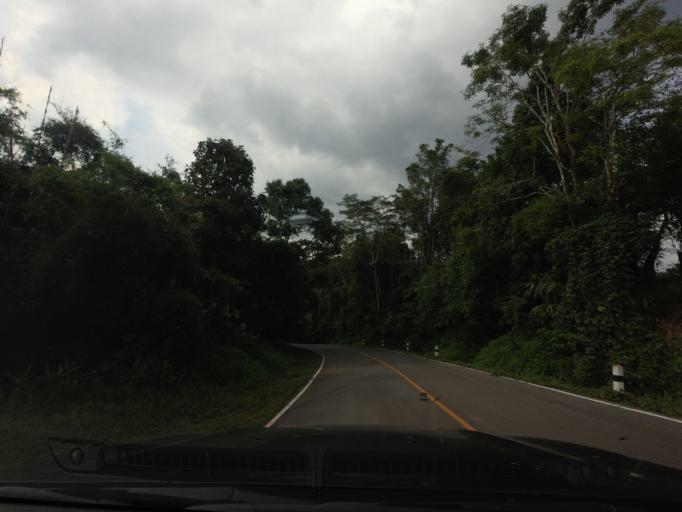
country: TH
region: Nan
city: Bo Kluea
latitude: 19.2665
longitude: 101.1780
